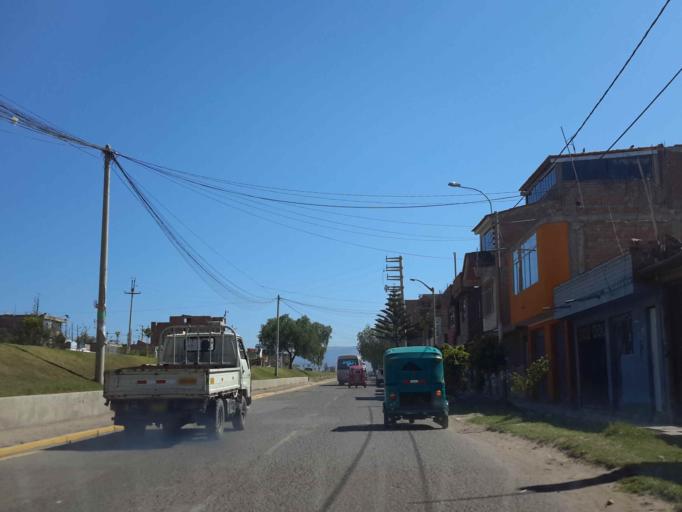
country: PE
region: Ayacucho
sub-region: Provincia de Huamanga
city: Ayacucho
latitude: -13.1393
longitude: -74.2287
